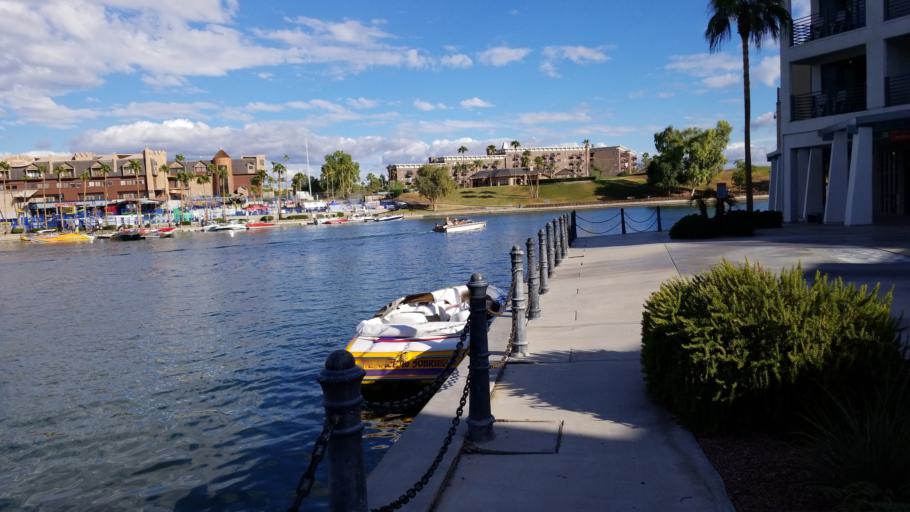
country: US
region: Arizona
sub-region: Mohave County
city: Lake Havasu City
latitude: 34.4709
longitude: -114.3480
